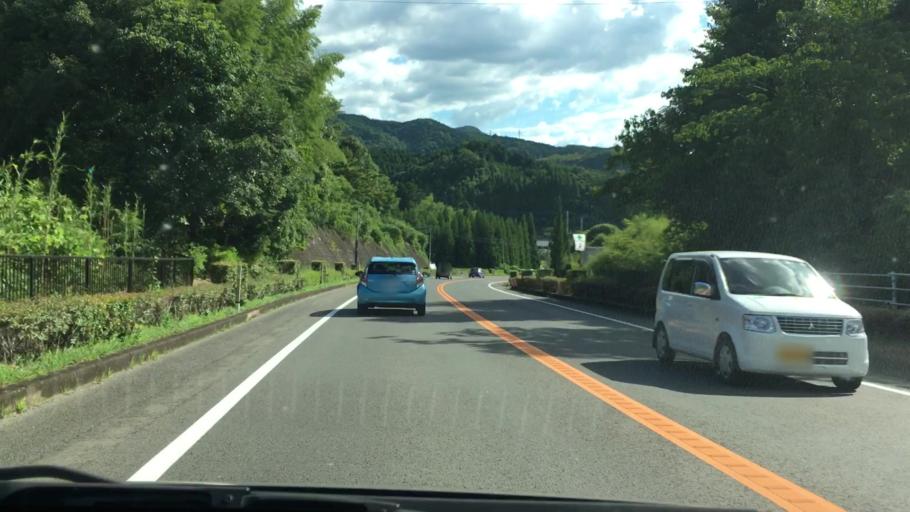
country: JP
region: Saga Prefecture
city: Takeocho-takeo
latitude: 33.1940
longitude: 129.9676
